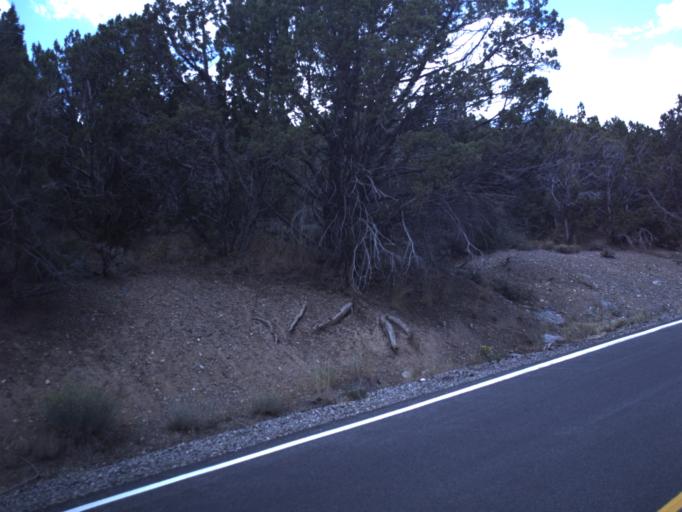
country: US
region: Utah
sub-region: Tooele County
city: Grantsville
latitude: 40.3395
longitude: -112.5747
